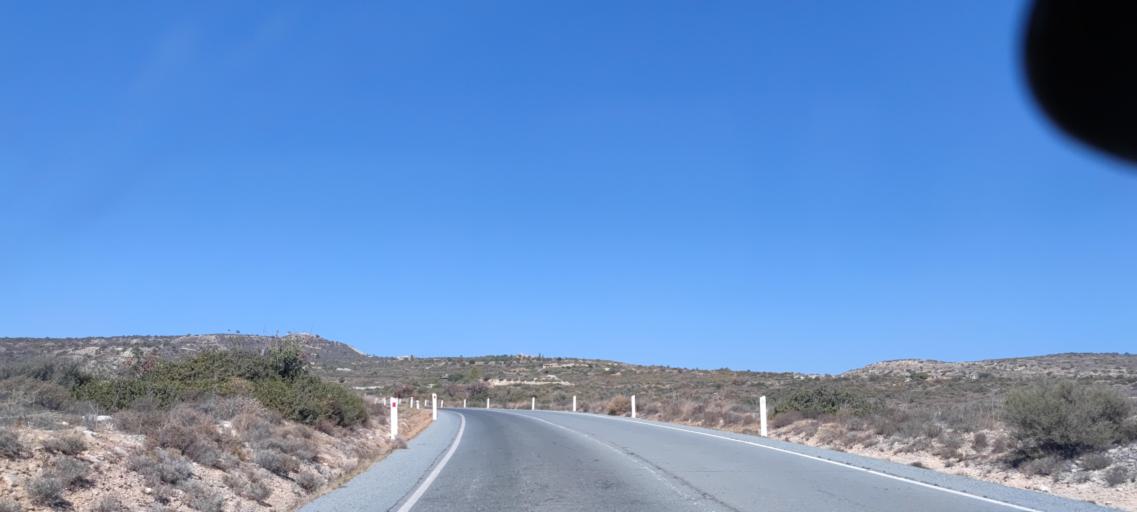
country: CY
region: Limassol
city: Mouttagiaka
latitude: 34.7370
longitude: 33.0644
